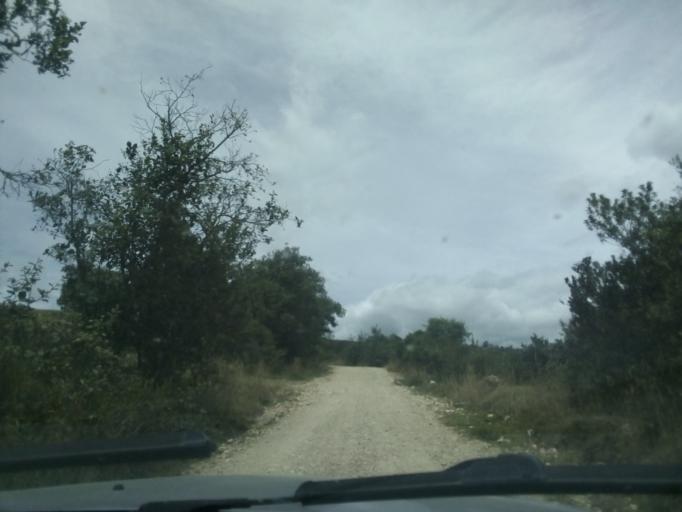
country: CO
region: Boyaca
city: Toca
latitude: 5.6218
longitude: -73.1262
